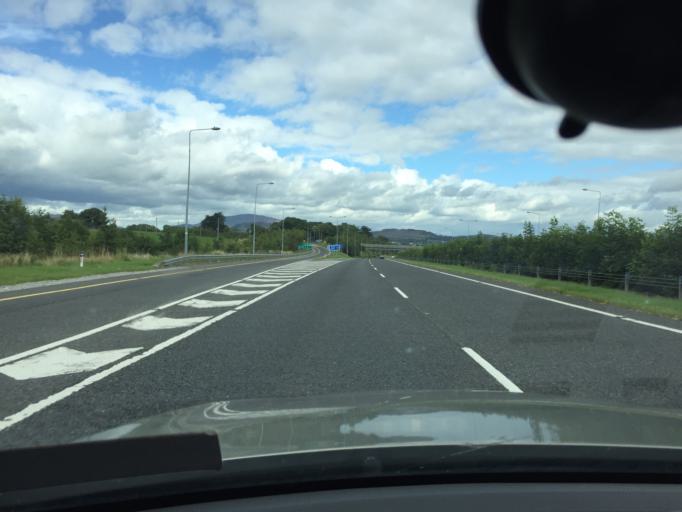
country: IE
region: Leinster
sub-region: Lu
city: Dundalk
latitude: 54.0151
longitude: -6.4449
